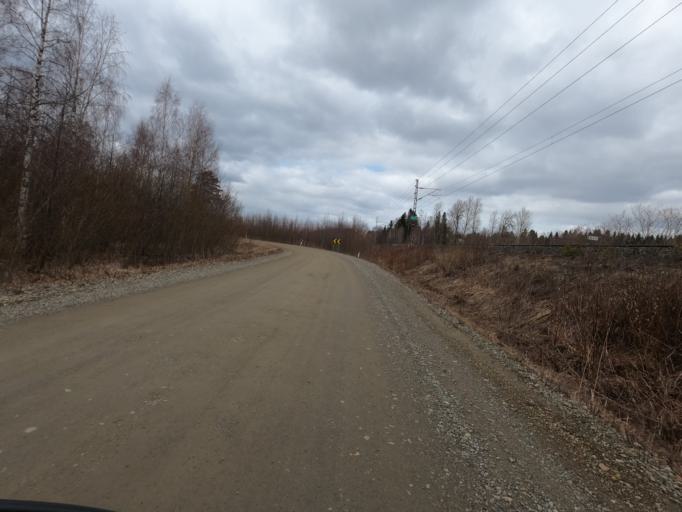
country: FI
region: North Karelia
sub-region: Joensuu
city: Joensuu
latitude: 62.5656
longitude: 29.8021
